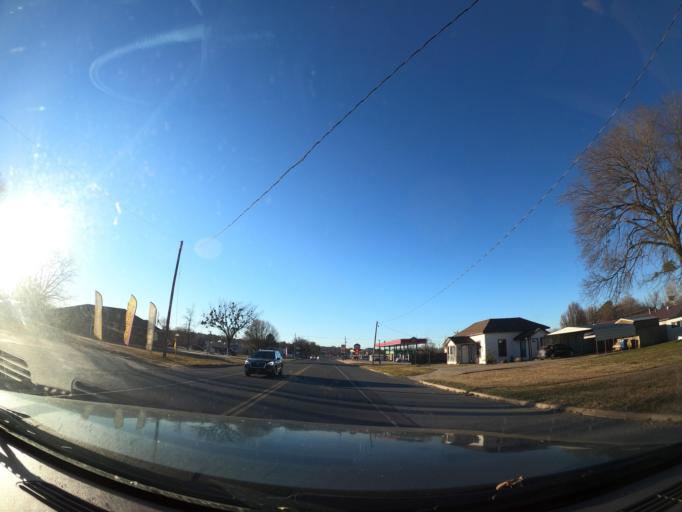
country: US
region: Oklahoma
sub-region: Pittsburg County
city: Hartshorne
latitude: 34.8462
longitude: -95.5601
